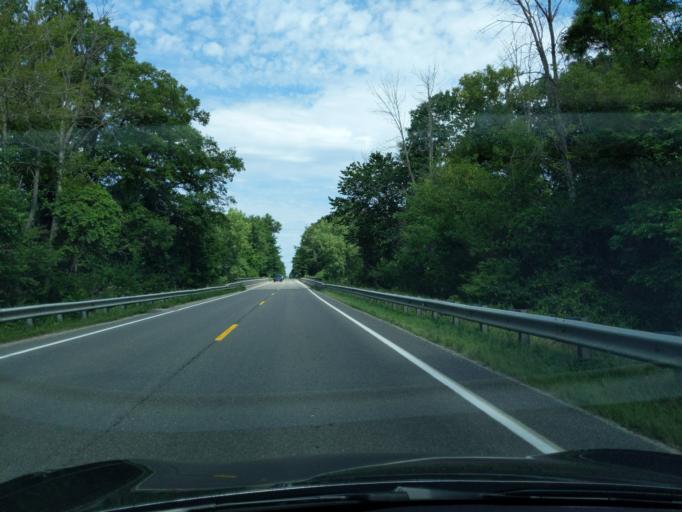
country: US
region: Michigan
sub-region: Midland County
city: Midland
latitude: 43.5937
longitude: -84.3693
